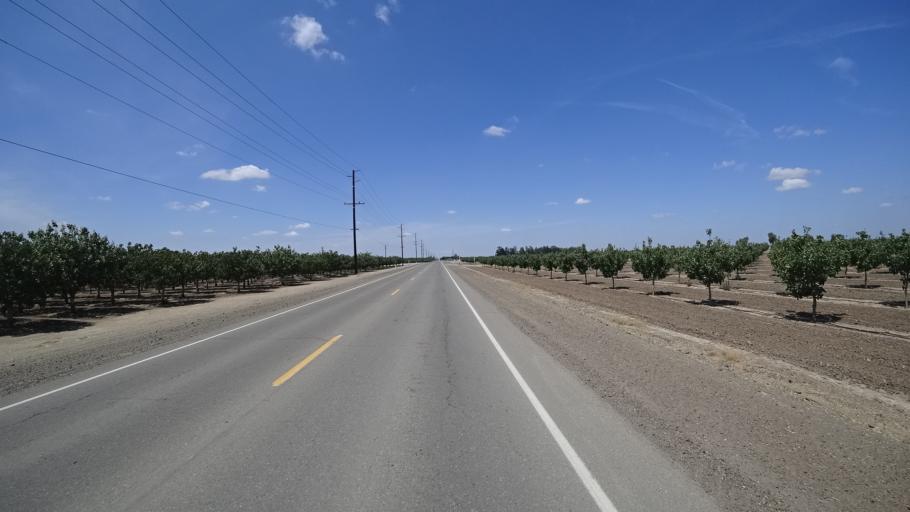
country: US
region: California
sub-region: Kings County
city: Home Garden
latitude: 36.2986
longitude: -119.5526
